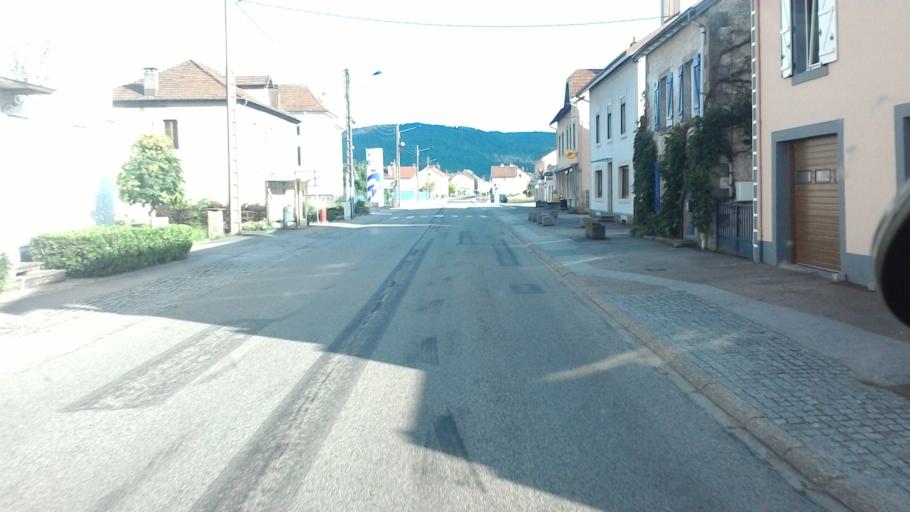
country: FR
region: Lorraine
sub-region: Departement des Vosges
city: Rupt-sur-Moselle
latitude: 47.9239
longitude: 6.6601
